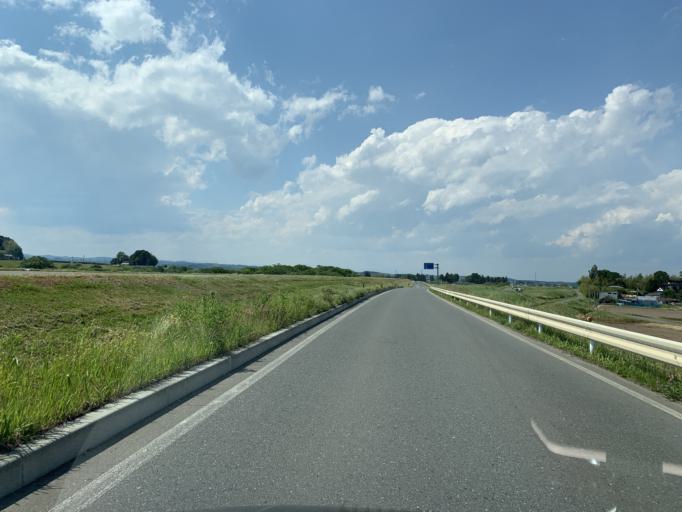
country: JP
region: Miyagi
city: Matsushima
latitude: 38.4373
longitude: 141.1182
